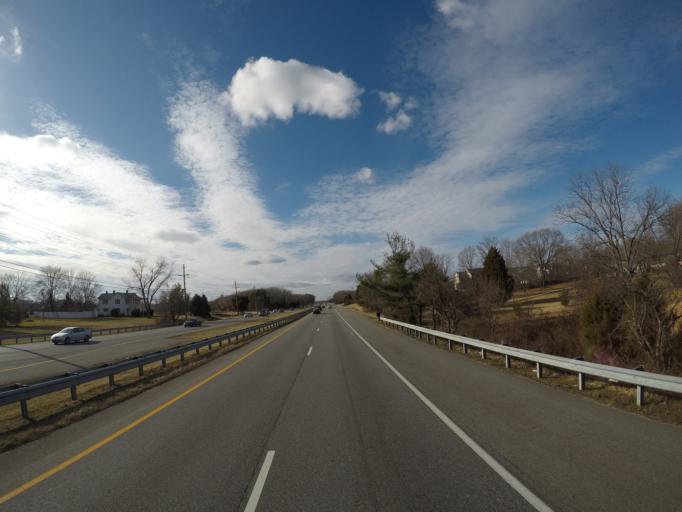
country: US
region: Maryland
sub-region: Charles County
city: Waldorf
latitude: 38.6494
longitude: -76.9583
